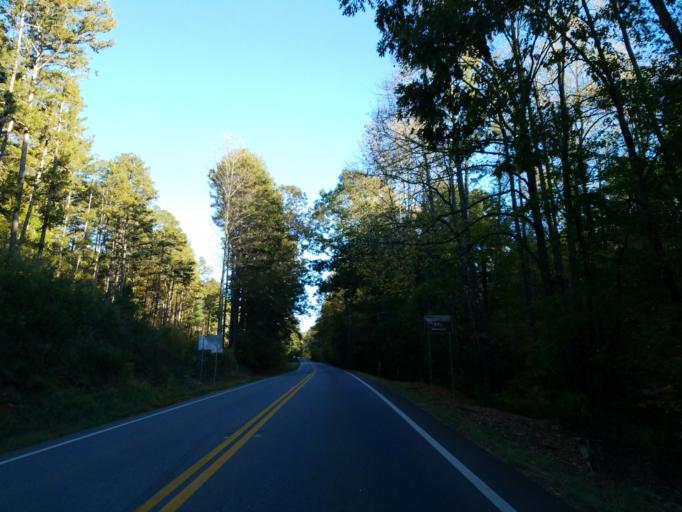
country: US
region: Georgia
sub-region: Dawson County
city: Dawsonville
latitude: 34.4245
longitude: -84.2086
